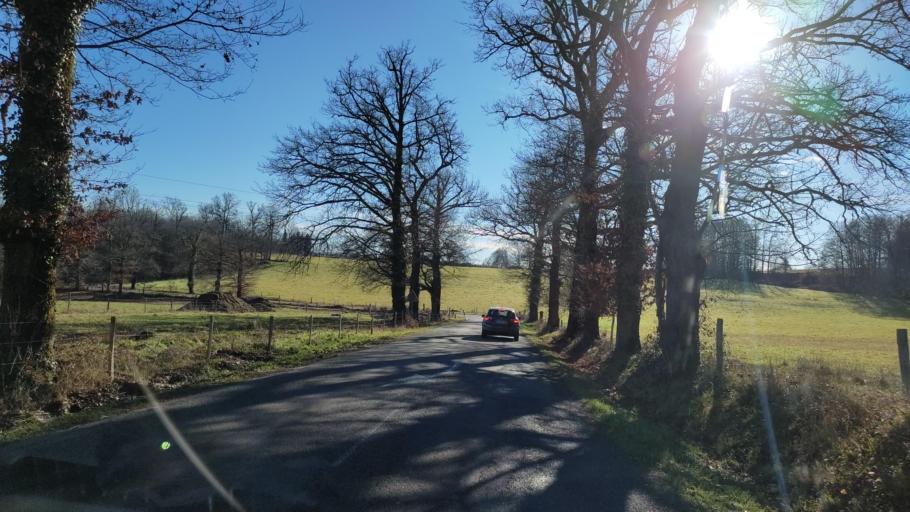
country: FR
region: Limousin
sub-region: Departement de la Haute-Vienne
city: Isle
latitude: 45.7969
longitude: 1.1995
